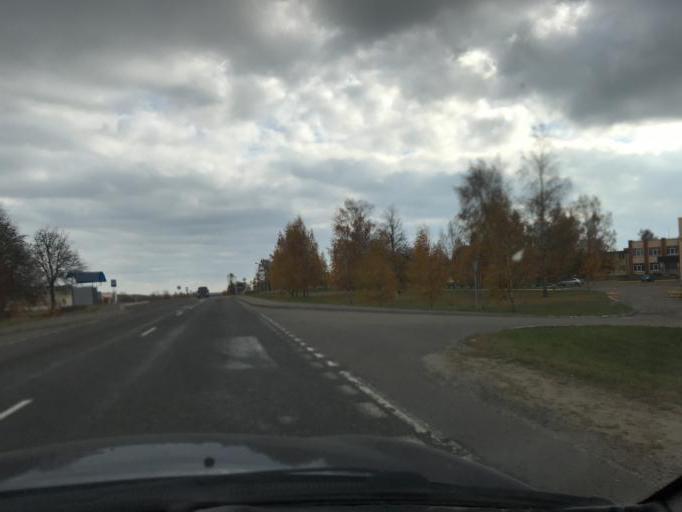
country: BY
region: Grodnenskaya
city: Lida
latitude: 53.7934
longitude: 25.1435
